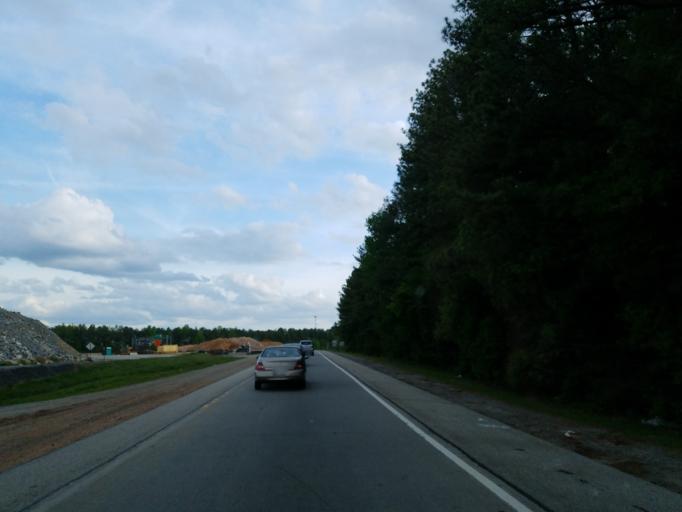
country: US
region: Georgia
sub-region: Cobb County
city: Marietta
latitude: 33.9852
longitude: -84.5450
